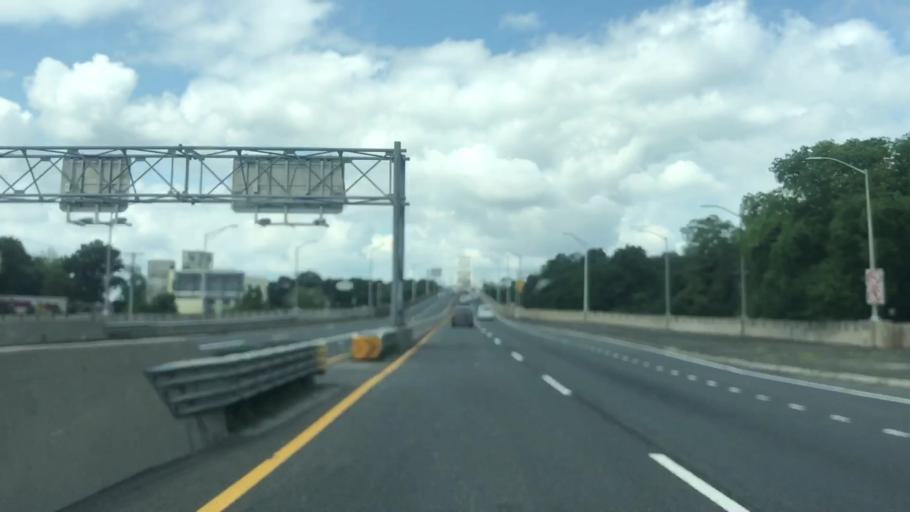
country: US
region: New Jersey
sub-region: Middlesex County
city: Perth Amboy
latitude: 40.5255
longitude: -74.2357
